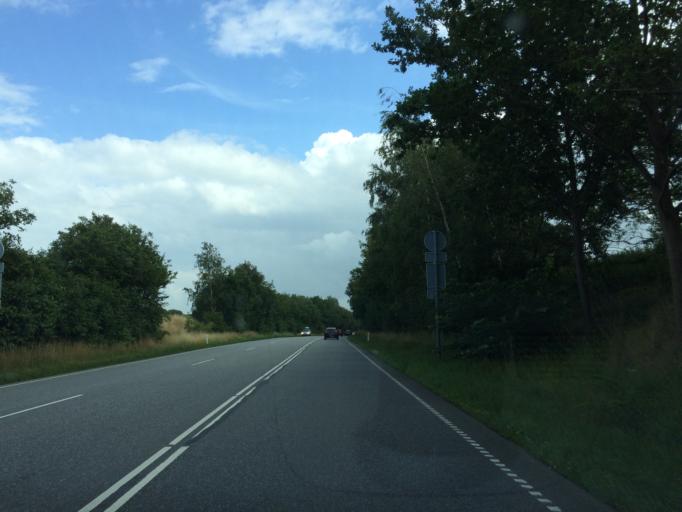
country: DK
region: Zealand
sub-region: Odsherred Kommune
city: Hojby
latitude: 55.9386
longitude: 11.5185
